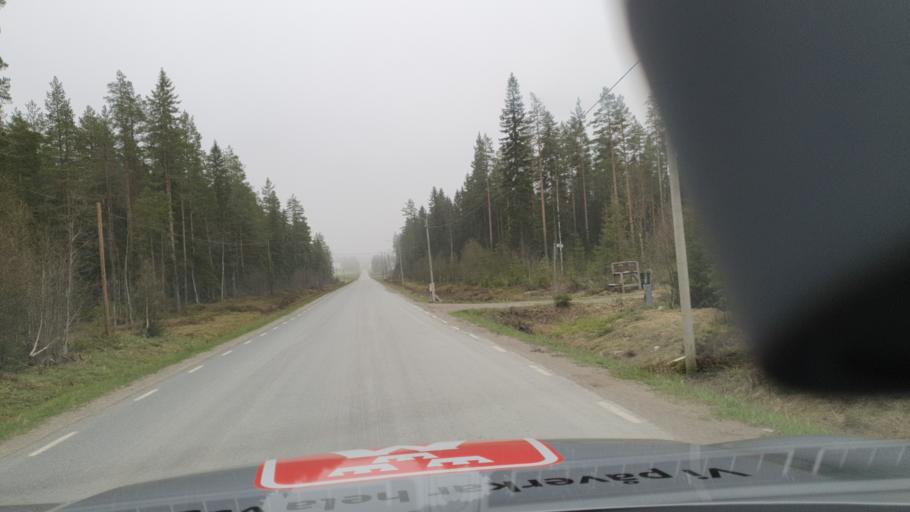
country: SE
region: Vaesternorrland
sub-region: OErnskoeldsviks Kommun
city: Husum
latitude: 63.5891
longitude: 19.0181
